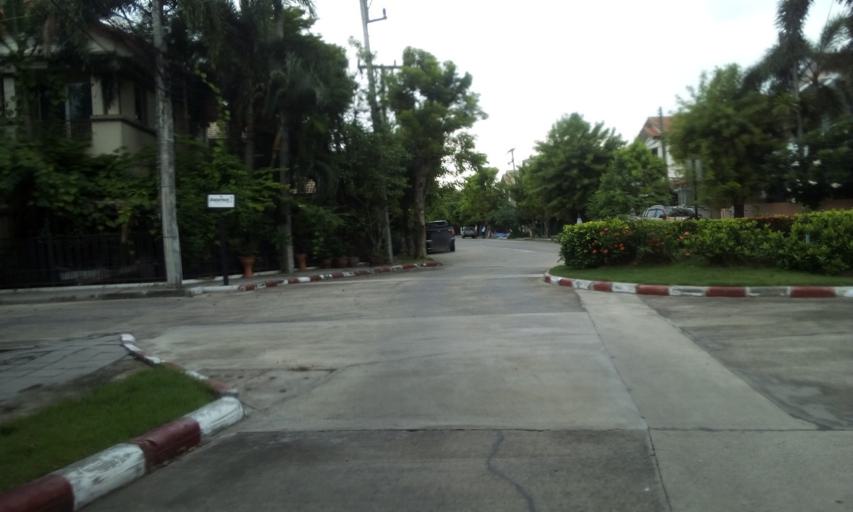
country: TH
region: Pathum Thani
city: Ban Rangsit
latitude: 14.0509
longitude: 100.8290
